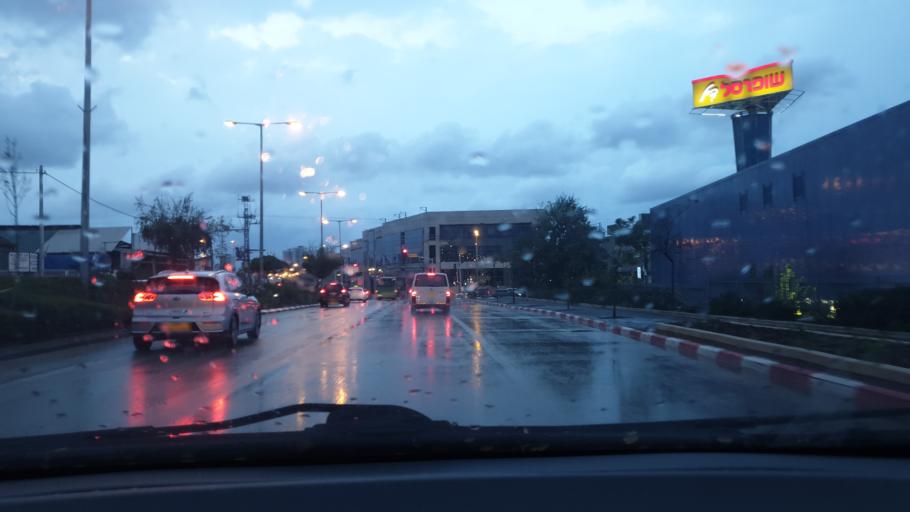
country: IL
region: Central District
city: Rishon LeZiyyon
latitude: 31.9758
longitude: 34.8125
